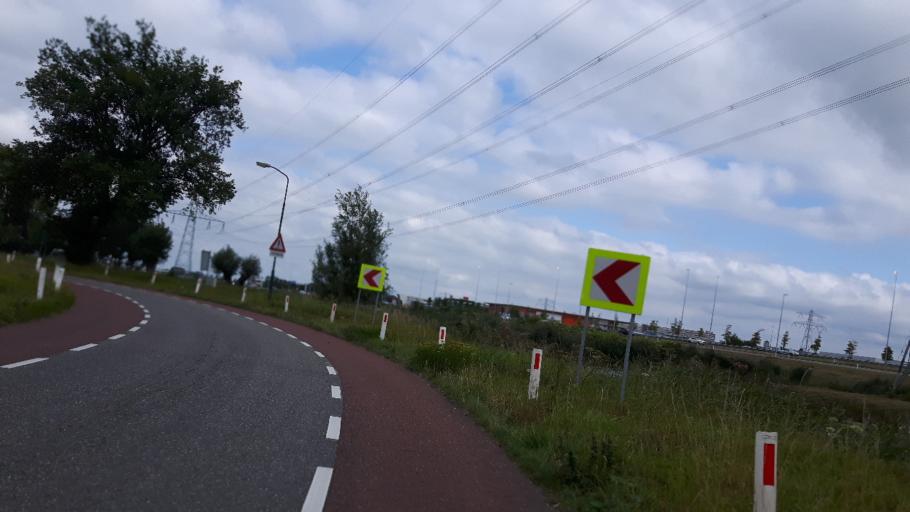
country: NL
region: Utrecht
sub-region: Stichtse Vecht
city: Breukelen
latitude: 52.1748
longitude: 4.9846
